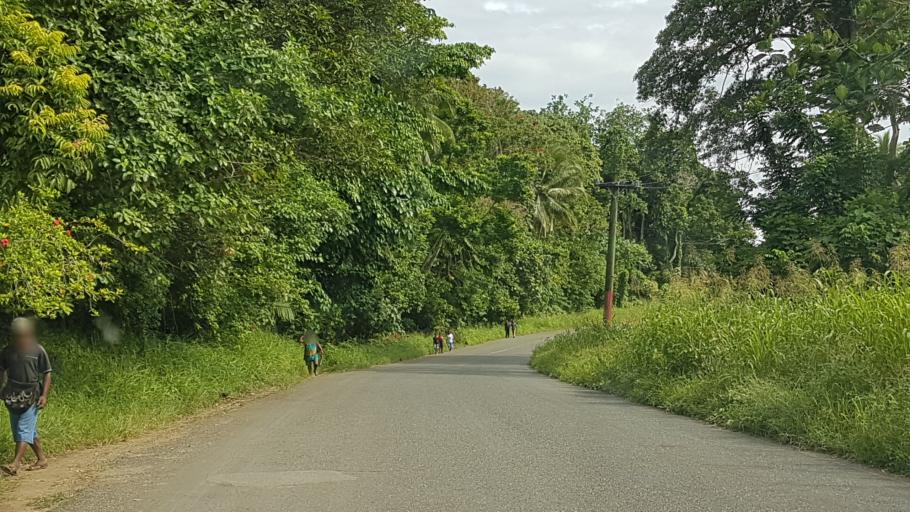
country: PG
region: Madang
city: Madang
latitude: -5.1983
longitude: 145.7742
